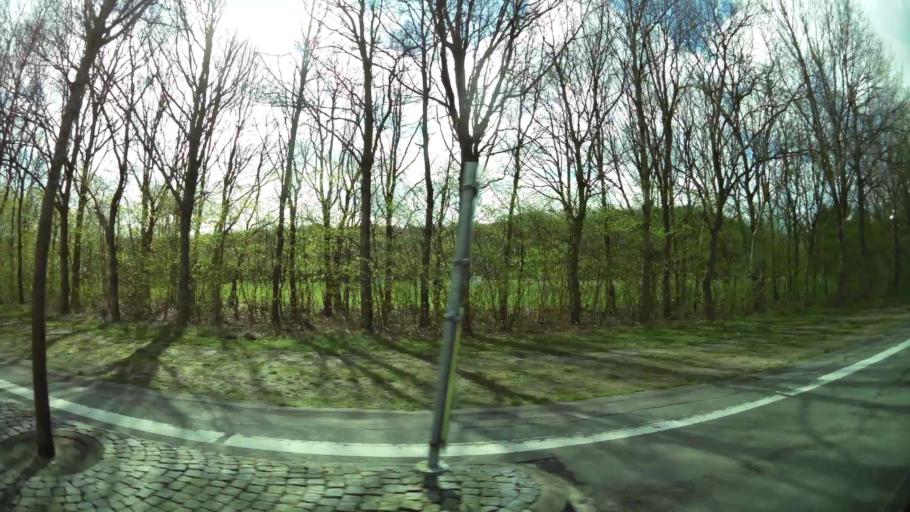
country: DK
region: North Denmark
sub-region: Mariagerfjord Kommune
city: Mariager
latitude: 56.6452
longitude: 9.9683
